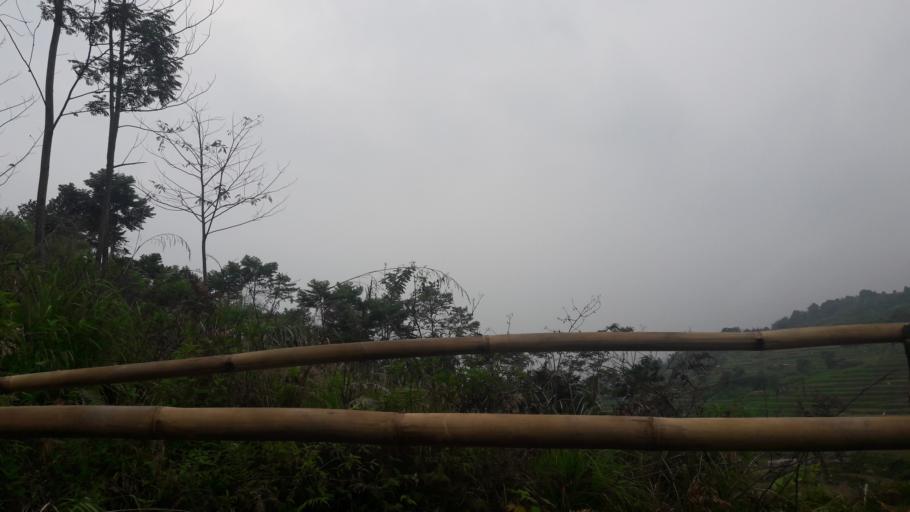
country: ID
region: West Java
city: Cipeundeuy
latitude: -6.6815
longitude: 106.5219
